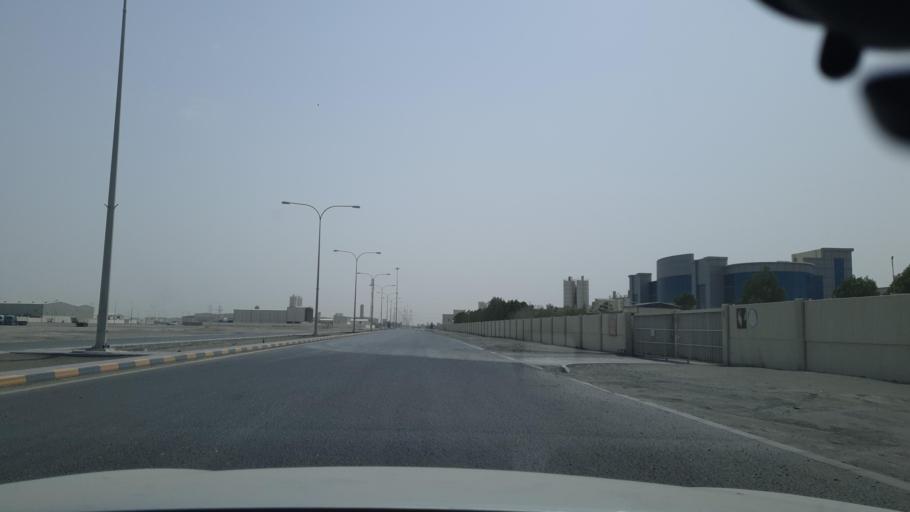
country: QA
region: Al Wakrah
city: Umm Sa'id
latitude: 25.0031
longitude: 51.5842
